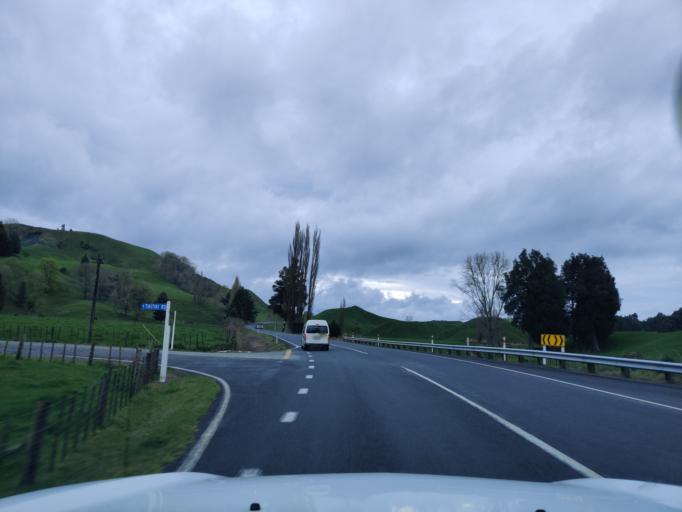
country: NZ
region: Waikato
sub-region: Otorohanga District
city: Otorohanga
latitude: -38.4732
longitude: 175.1738
